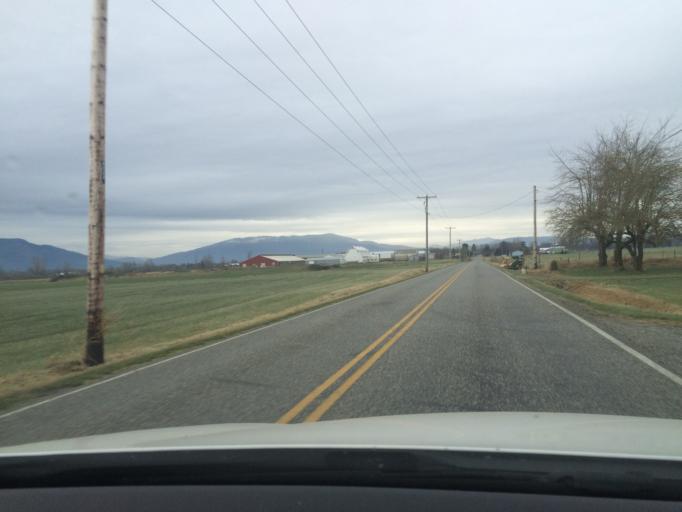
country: US
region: Washington
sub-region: Whatcom County
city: Everson
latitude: 48.9390
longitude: -122.3524
